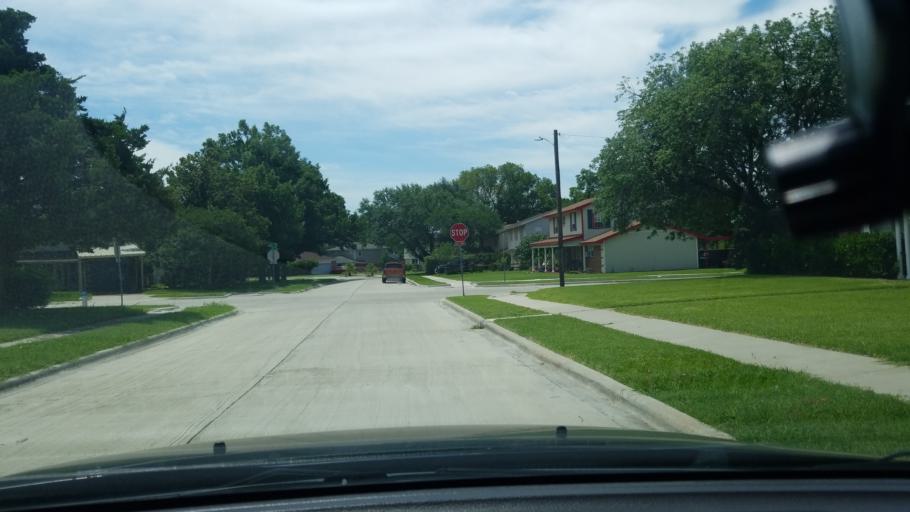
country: US
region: Texas
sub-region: Dallas County
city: Mesquite
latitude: 32.8037
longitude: -96.6563
